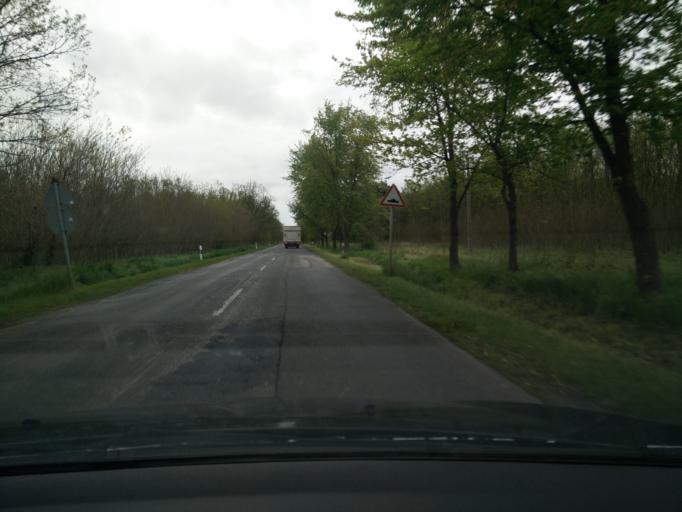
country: HU
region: Gyor-Moson-Sopron
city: Gyorszemere
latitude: 47.5423
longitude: 17.5463
